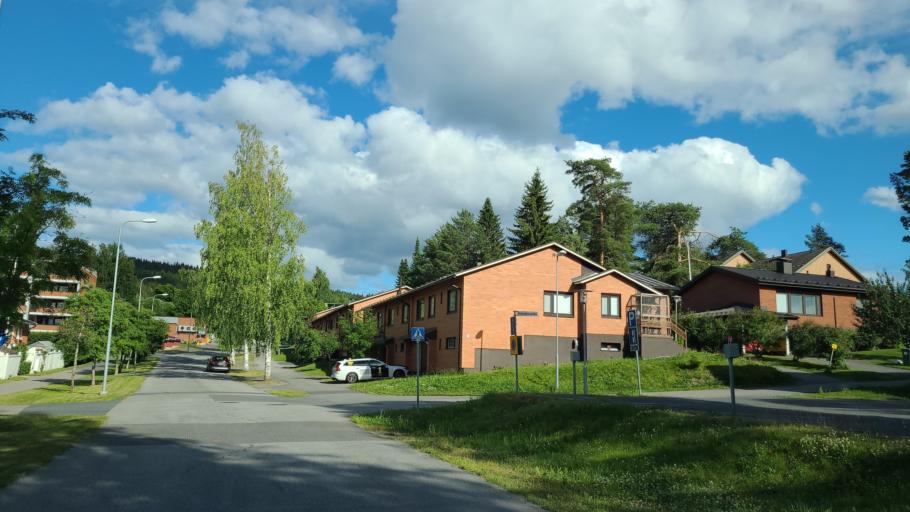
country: FI
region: Northern Savo
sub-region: Kuopio
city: Kuopio
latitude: 62.9259
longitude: 27.6279
